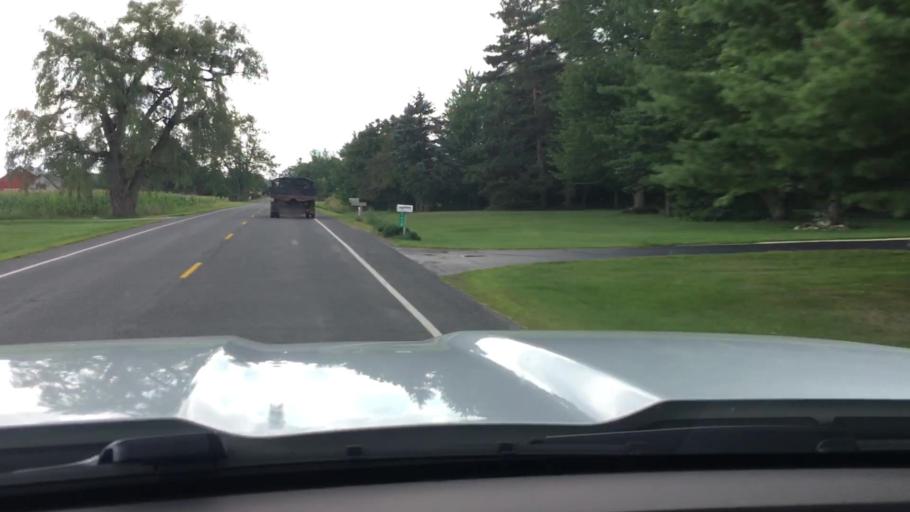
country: US
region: Michigan
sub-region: Eaton County
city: Eaton Rapids
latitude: 42.5404
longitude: -84.5620
